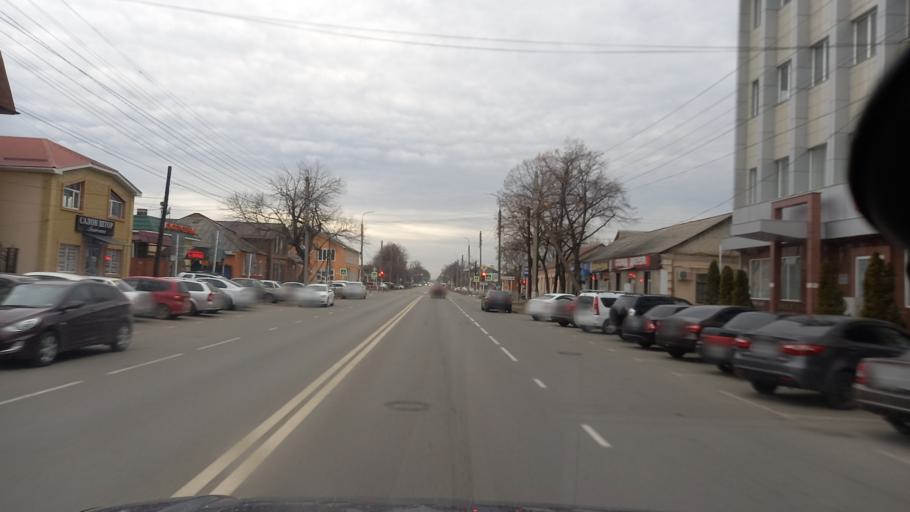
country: RU
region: Adygeya
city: Maykop
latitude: 44.6129
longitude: 40.1026
